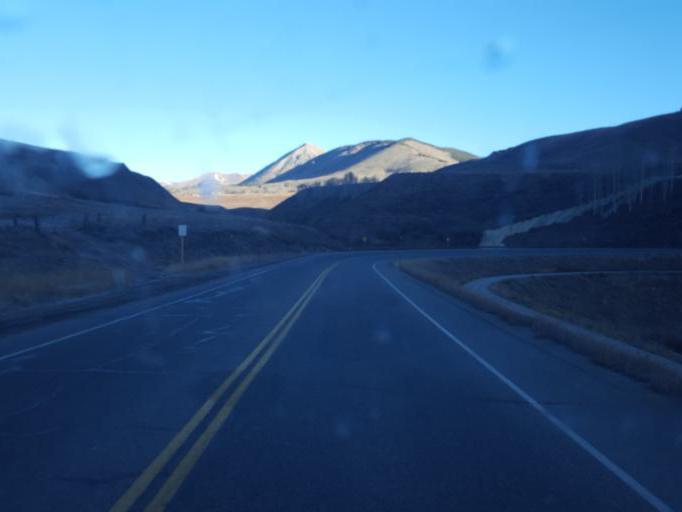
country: US
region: Colorado
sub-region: Gunnison County
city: Crested Butte
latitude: 38.8910
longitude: -106.9730
